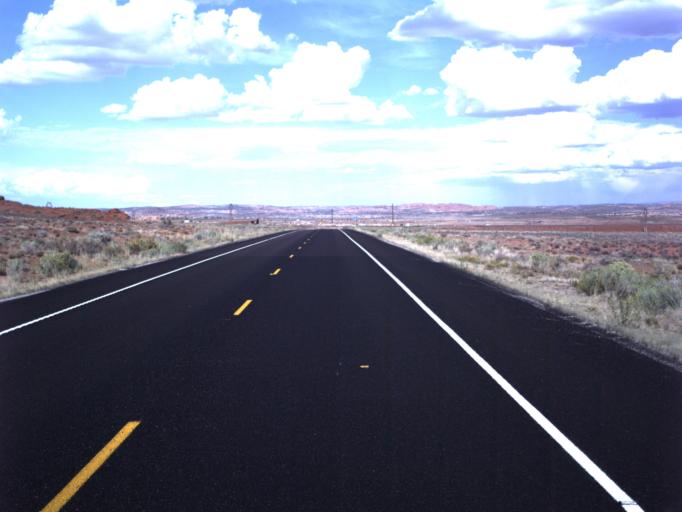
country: US
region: Utah
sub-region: Grand County
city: Moab
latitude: 38.6650
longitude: -109.6993
